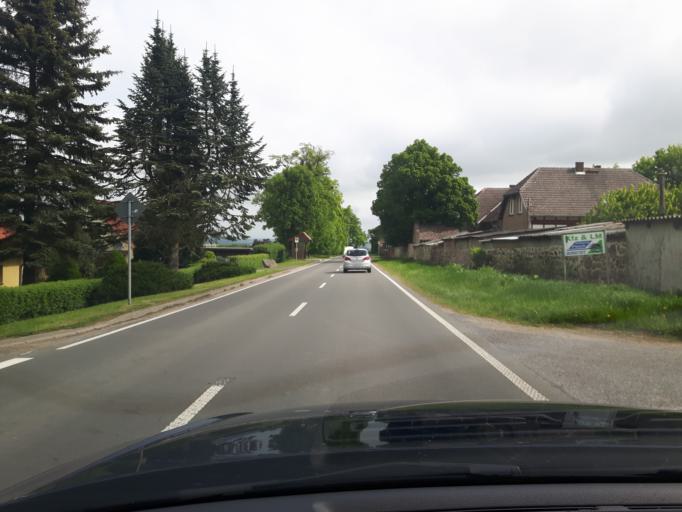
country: DE
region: Mecklenburg-Vorpommern
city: Gross Wokern
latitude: 53.6431
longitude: 12.4878
